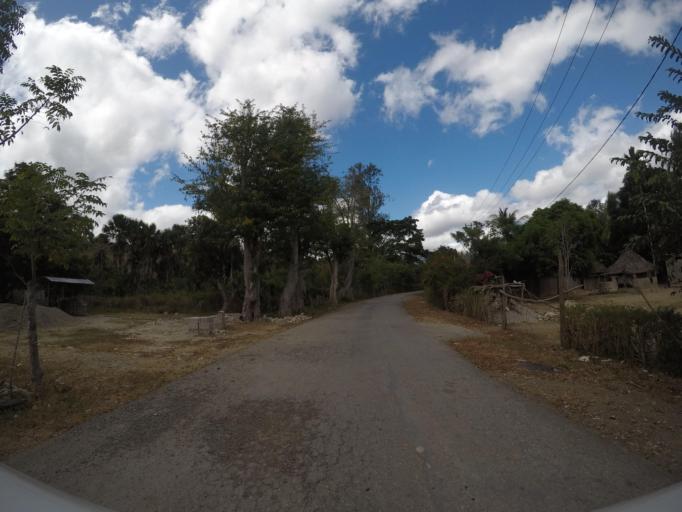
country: TL
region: Lautem
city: Lospalos
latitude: -8.4554
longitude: 126.8220
